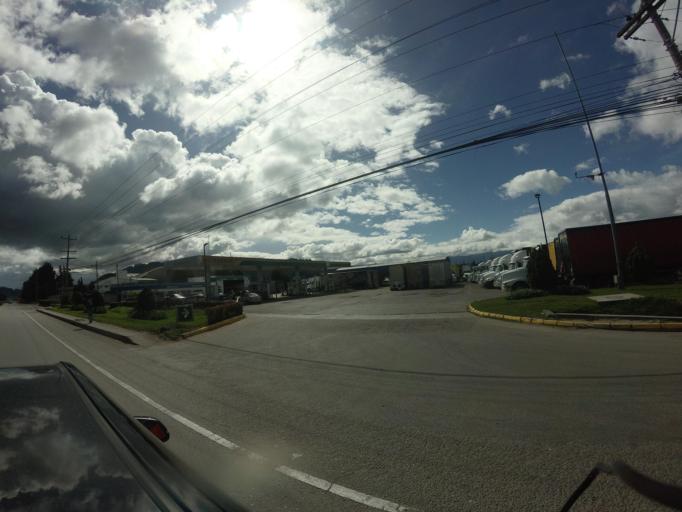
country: CO
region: Cundinamarca
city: Tocancipa
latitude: 4.9500
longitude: -73.9458
